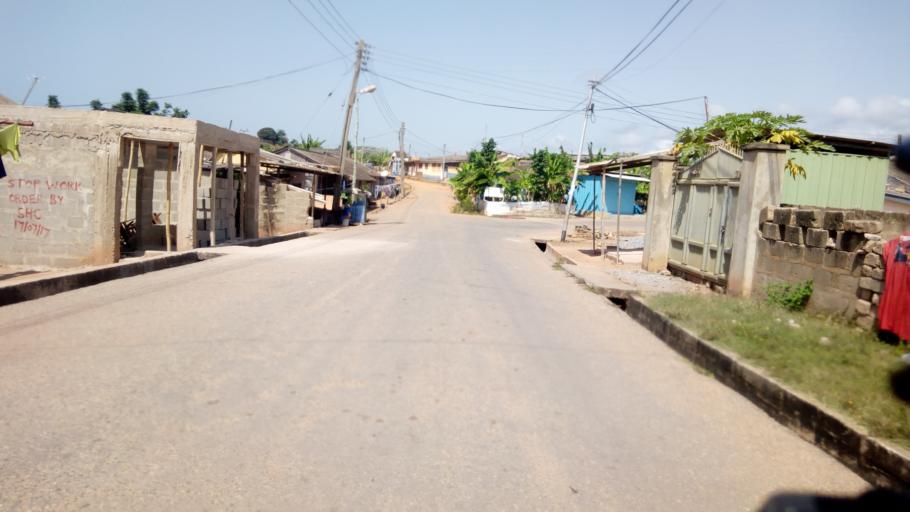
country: GH
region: Central
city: Cape Coast
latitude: 5.1126
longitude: -1.2642
